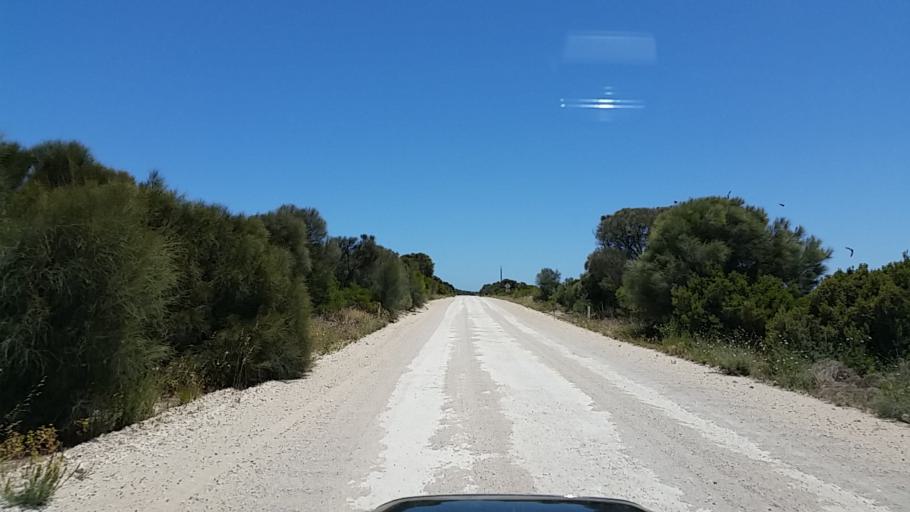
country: AU
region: South Australia
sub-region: Yorke Peninsula
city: Honiton
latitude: -35.2218
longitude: 137.0732
